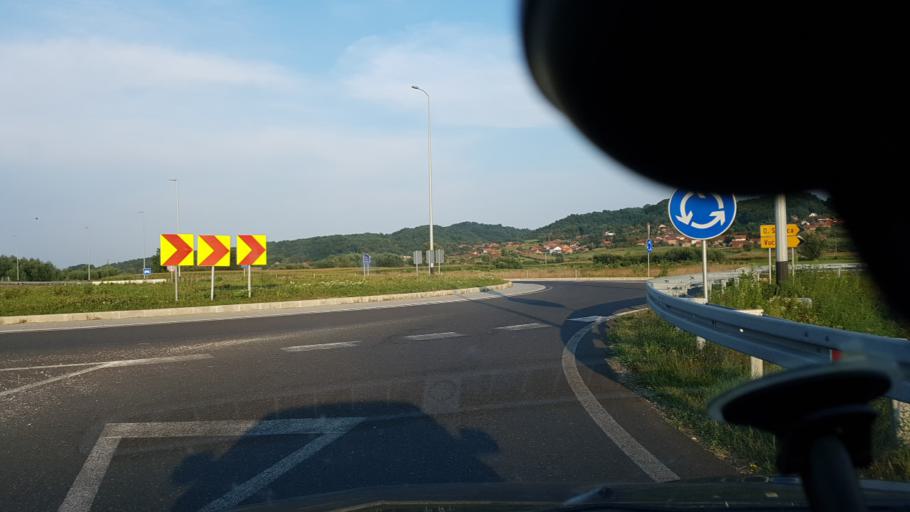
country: HR
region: Krapinsko-Zagorska
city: Bedekovcina
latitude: 46.0314
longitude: 15.9934
